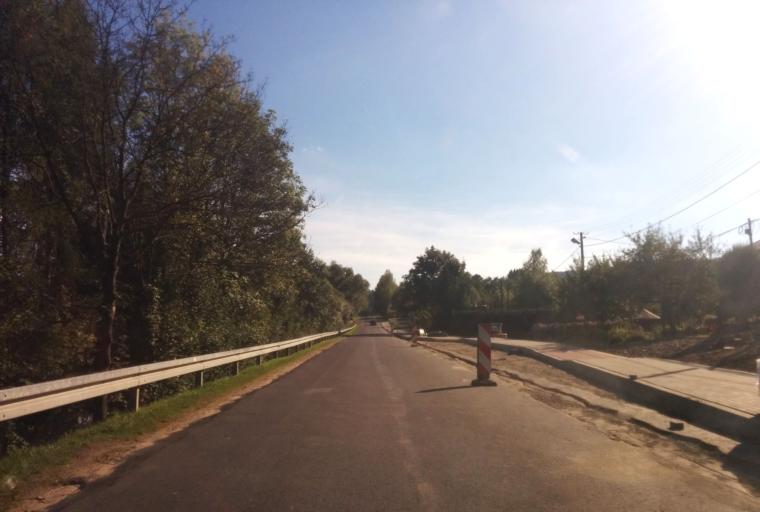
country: PL
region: Subcarpathian Voivodeship
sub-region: Powiat leski
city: Polanczyk
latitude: 49.3122
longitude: 22.4107
